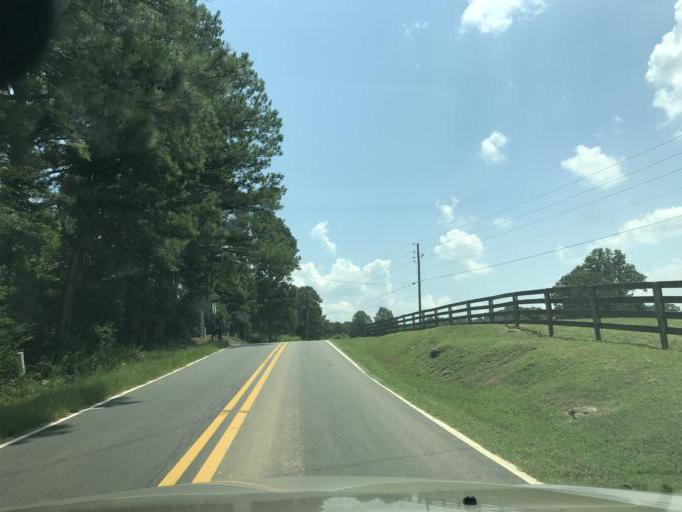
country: US
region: Georgia
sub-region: Forsyth County
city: Cumming
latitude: 34.3106
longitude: -84.1948
